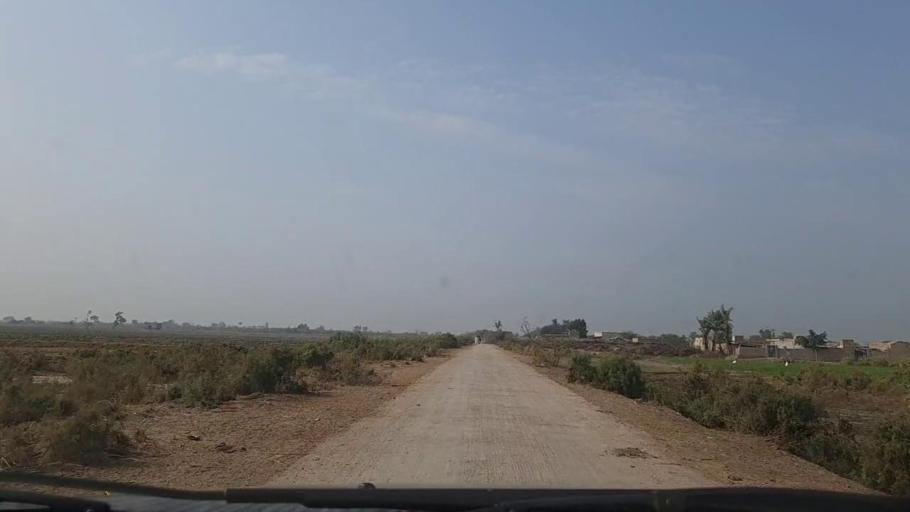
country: PK
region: Sindh
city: Sanghar
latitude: 26.0753
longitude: 68.9530
